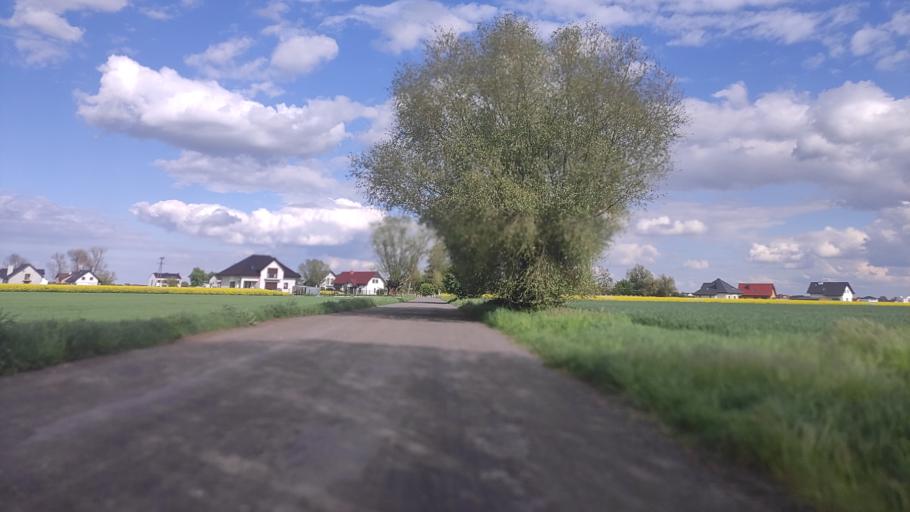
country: PL
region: Greater Poland Voivodeship
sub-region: Powiat poznanski
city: Kleszczewo
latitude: 52.3863
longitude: 17.1409
